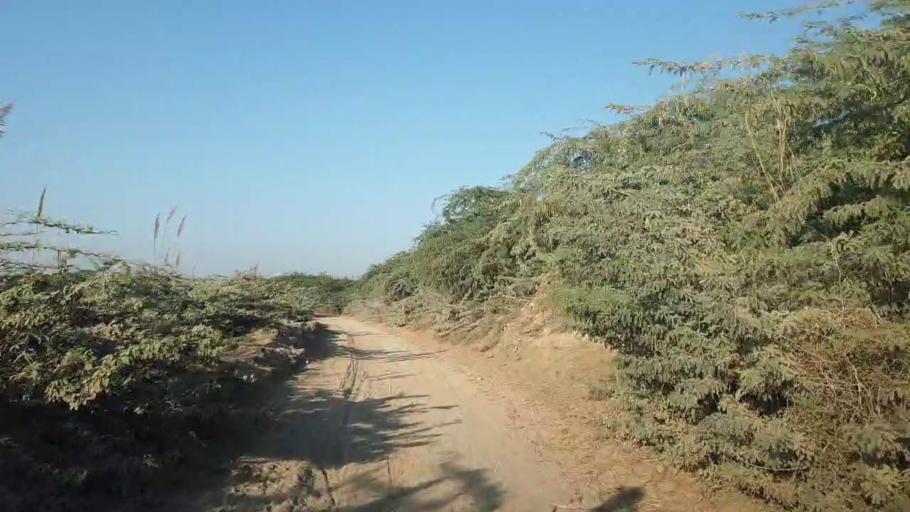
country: PK
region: Sindh
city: Mirpur Sakro
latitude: 24.5306
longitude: 67.5270
